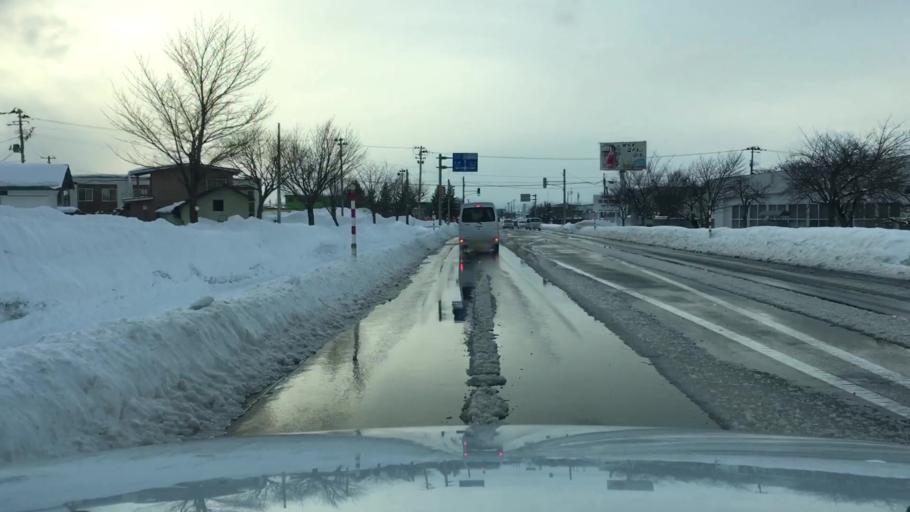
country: JP
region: Aomori
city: Hirosaki
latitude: 40.5945
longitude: 140.5366
